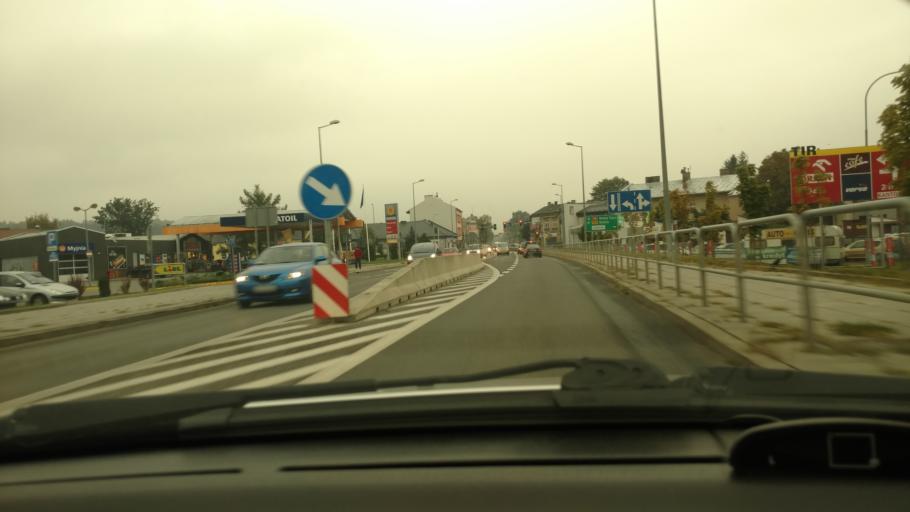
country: PL
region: Lesser Poland Voivodeship
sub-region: Powiat gorlicki
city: Gorlice
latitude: 49.6560
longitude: 21.1612
